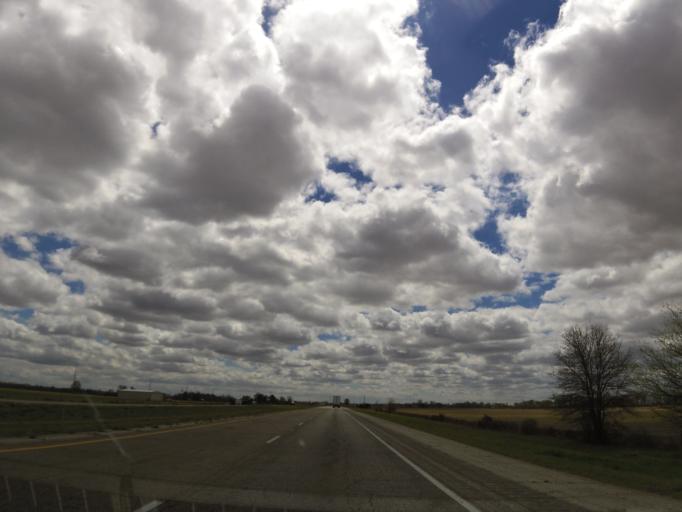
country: US
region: Arkansas
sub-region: Poinsett County
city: Marked Tree
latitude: 35.5757
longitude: -90.4969
